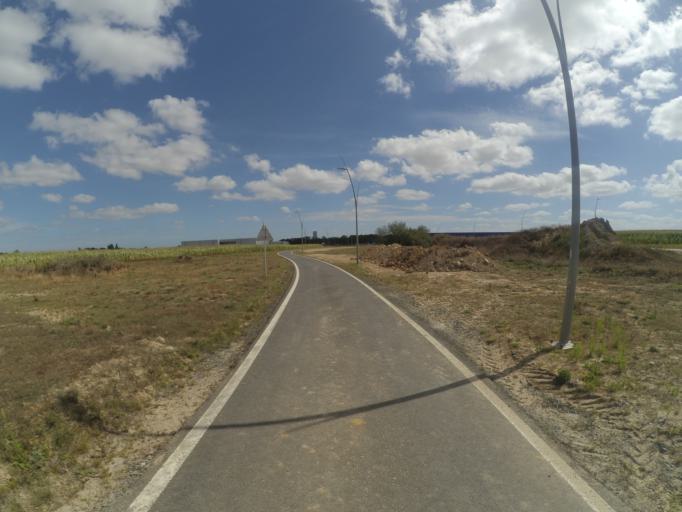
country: FR
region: Pays de la Loire
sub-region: Departement de la Vendee
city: Saint-Hilaire-de-Loulay
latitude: 47.0248
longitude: -1.3524
